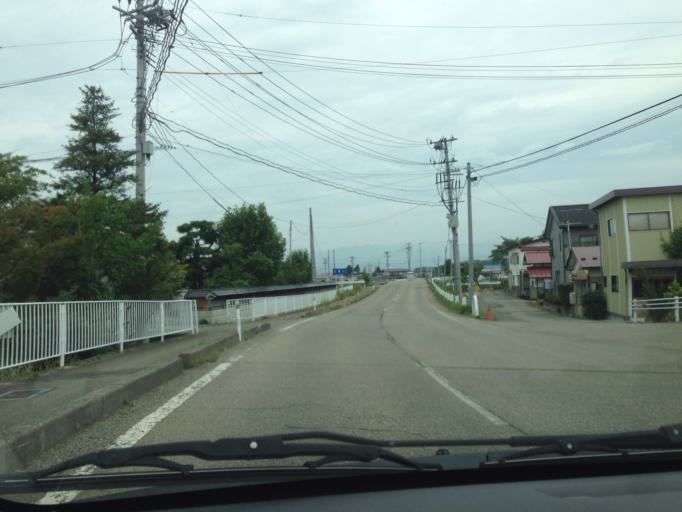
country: JP
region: Fukushima
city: Kitakata
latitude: 37.5803
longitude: 139.9131
